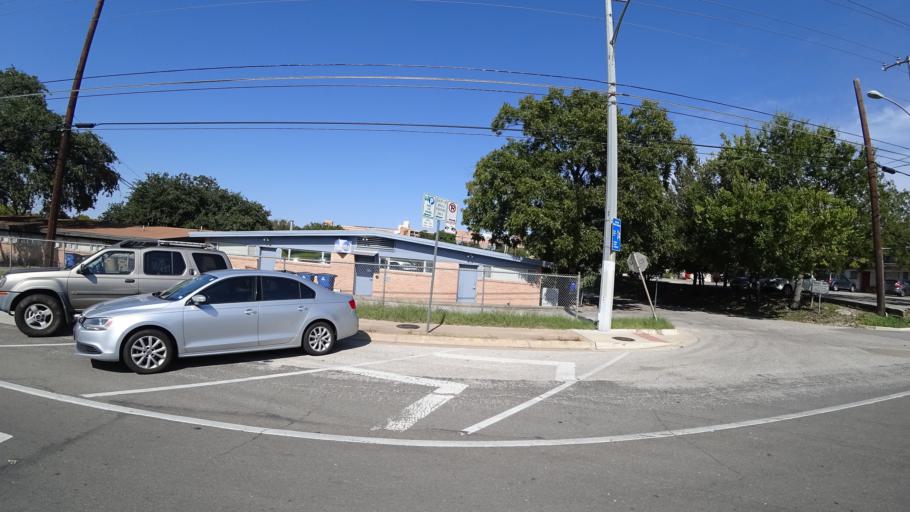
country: US
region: Texas
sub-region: Travis County
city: Austin
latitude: 30.2876
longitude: -97.7275
